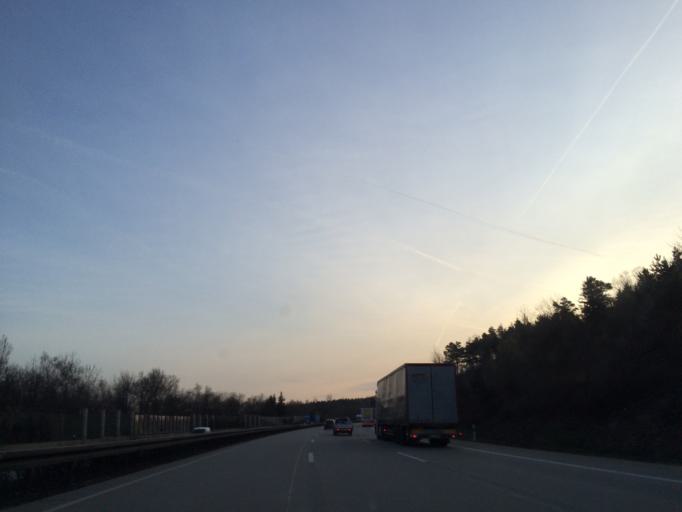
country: DE
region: Thuringia
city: Hainspitz
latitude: 50.9538
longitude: 11.8384
